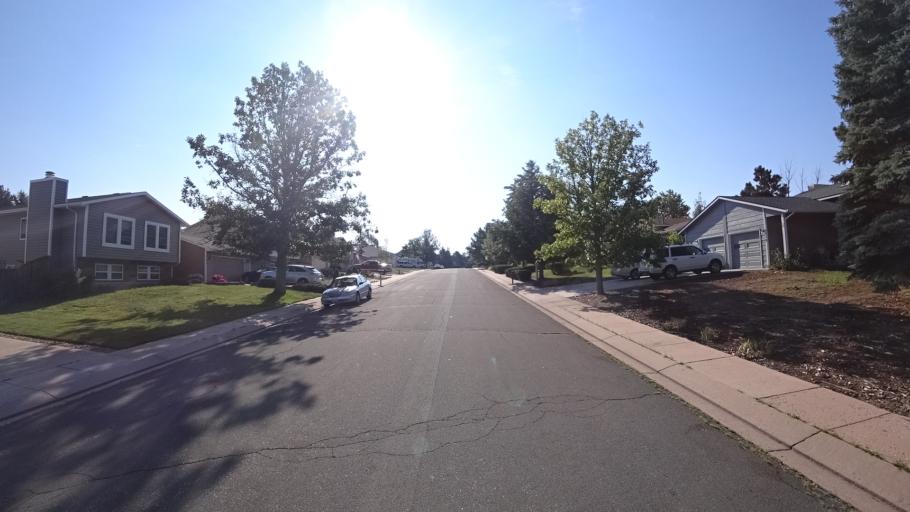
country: US
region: Colorado
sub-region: El Paso County
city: Air Force Academy
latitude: 38.9457
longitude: -104.7775
